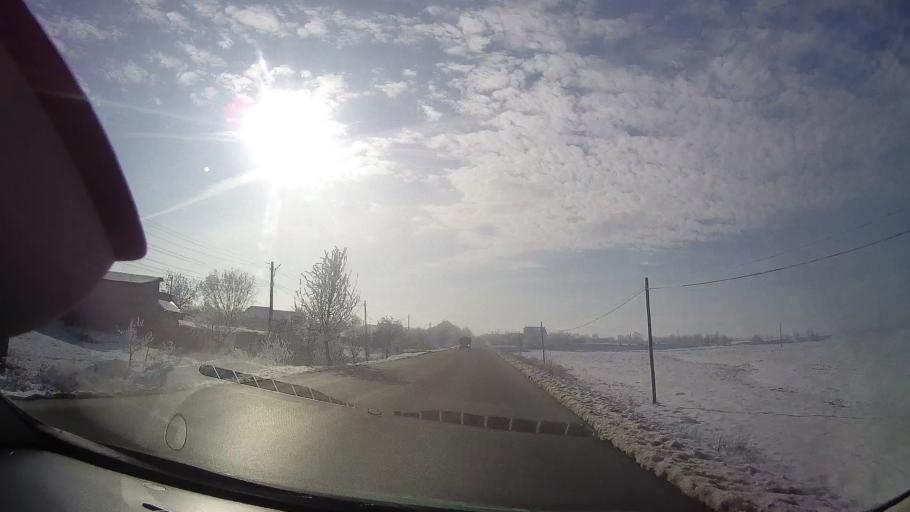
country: RO
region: Neamt
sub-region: Comuna Timisesti
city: Timisesti
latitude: 47.2387
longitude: 26.5376
